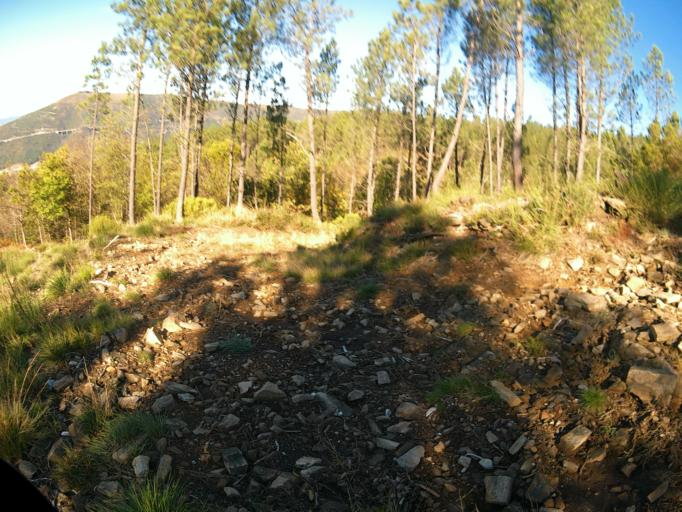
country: PT
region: Vila Real
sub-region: Mesao Frio
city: Mesao Frio
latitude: 41.2432
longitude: -7.9321
